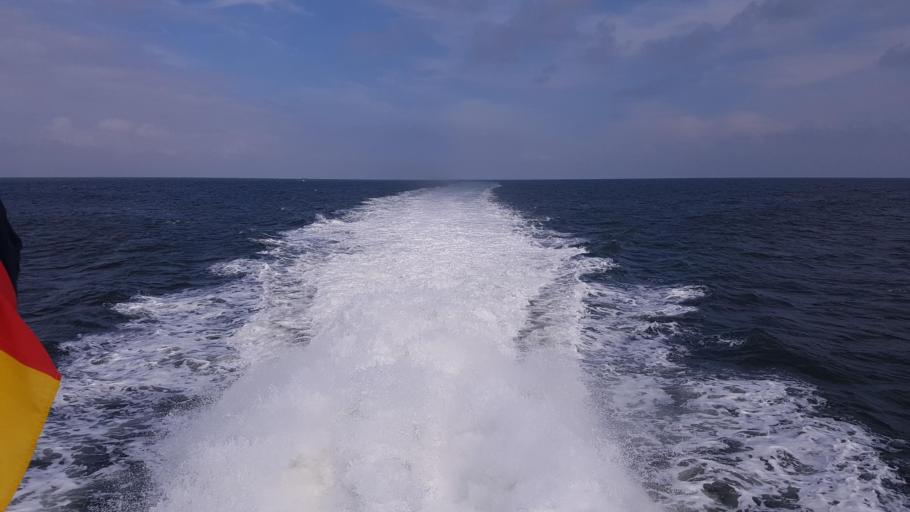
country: DE
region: Schleswig-Holstein
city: Hooge
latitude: 54.5832
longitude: 8.5759
